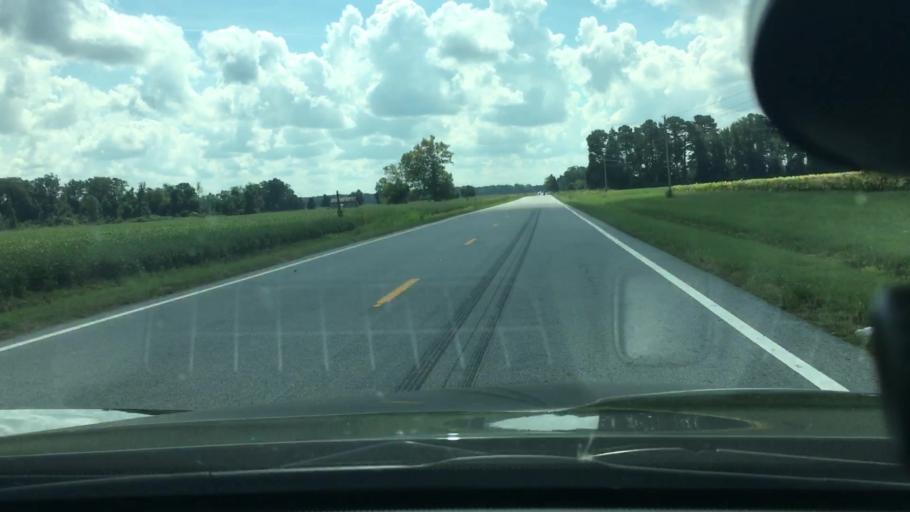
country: US
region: North Carolina
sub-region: Pitt County
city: Summerfield
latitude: 35.6660
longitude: -77.4776
